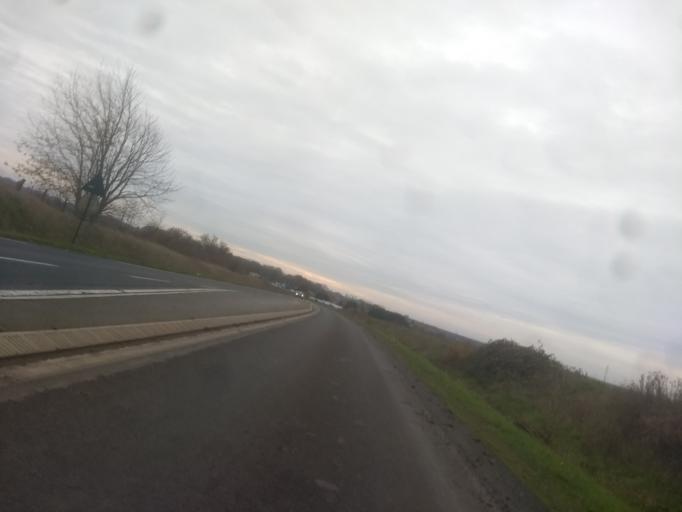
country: FR
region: Nord-Pas-de-Calais
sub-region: Departement du Pas-de-Calais
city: Achicourt
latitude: 50.2712
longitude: 2.7458
